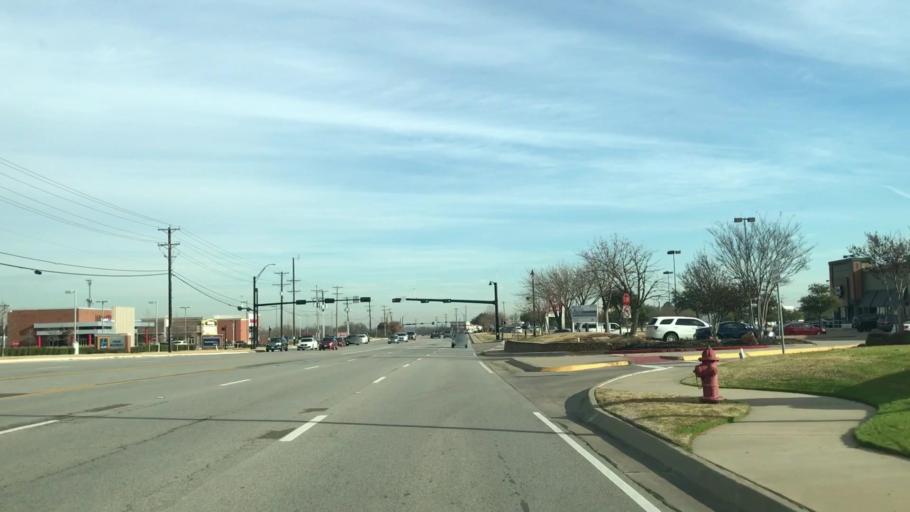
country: US
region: Texas
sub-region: Tarrant County
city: Colleyville
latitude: 32.9075
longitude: -97.1909
